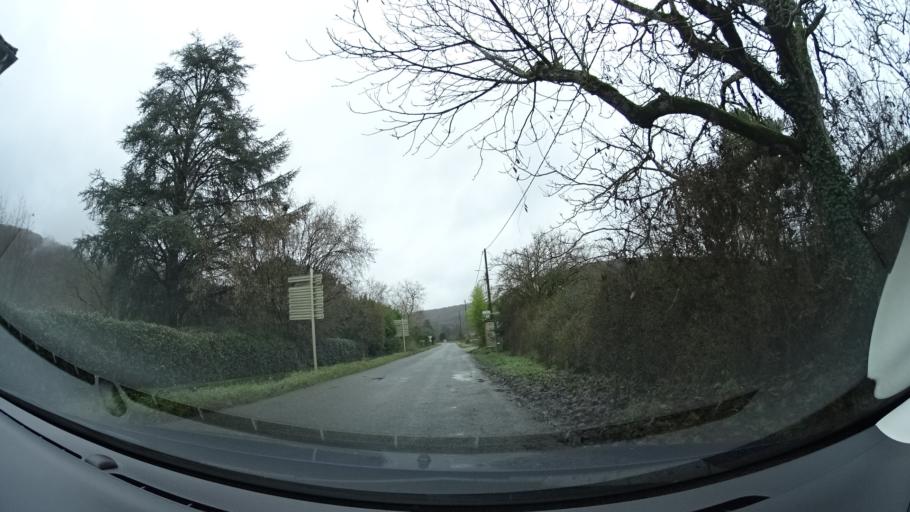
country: FR
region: Midi-Pyrenees
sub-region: Departement du Lot
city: Prayssac
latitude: 44.4960
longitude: 1.2158
